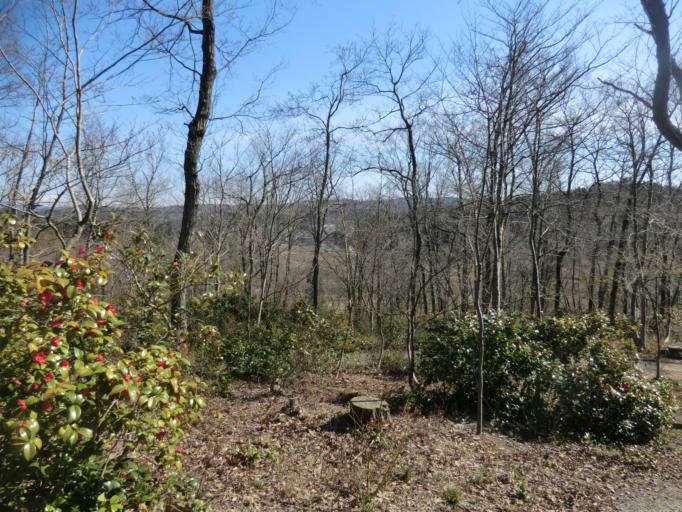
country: JP
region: Niigata
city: Nagaoka
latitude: 37.4639
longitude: 138.7435
